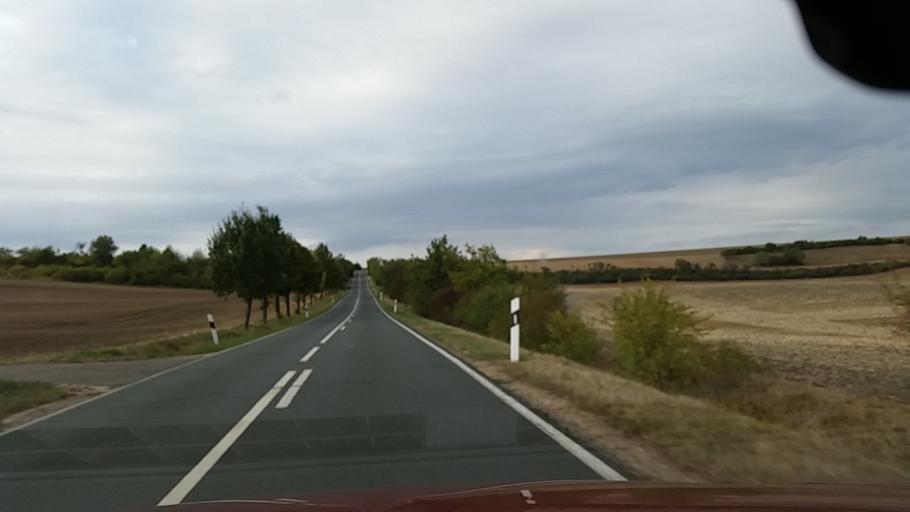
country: DE
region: Thuringia
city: Beichlingen
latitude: 51.2158
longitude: 11.2545
